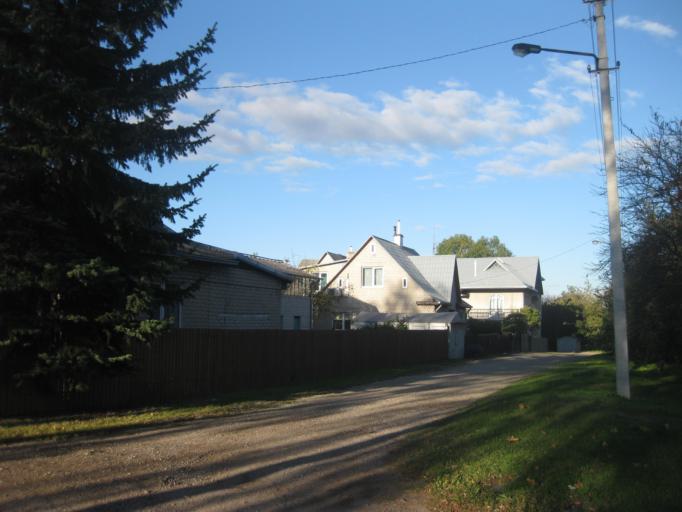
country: LT
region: Kauno apskritis
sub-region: Kaunas
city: Aleksotas
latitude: 54.8870
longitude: 23.8997
